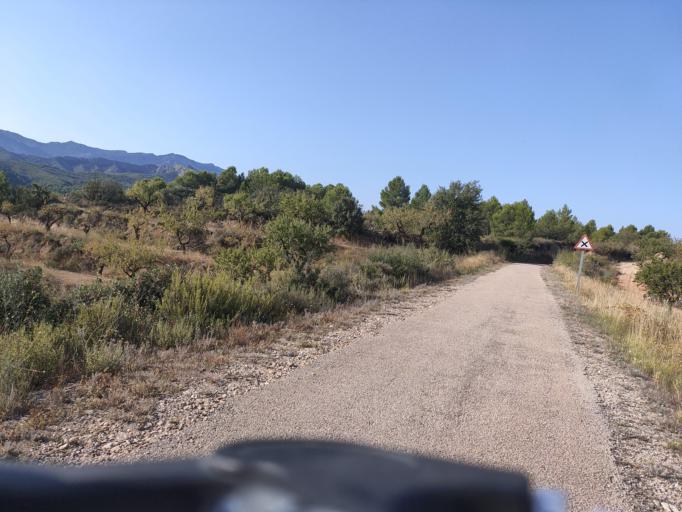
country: ES
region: Catalonia
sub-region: Provincia de Tarragona
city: Bot
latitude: 41.0013
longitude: 0.3731
